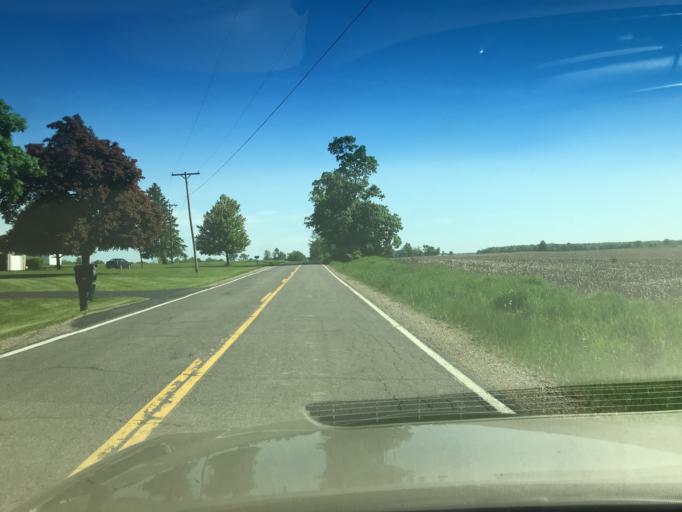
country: US
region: Michigan
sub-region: Ingham County
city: Mason
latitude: 42.5315
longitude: -84.4625
